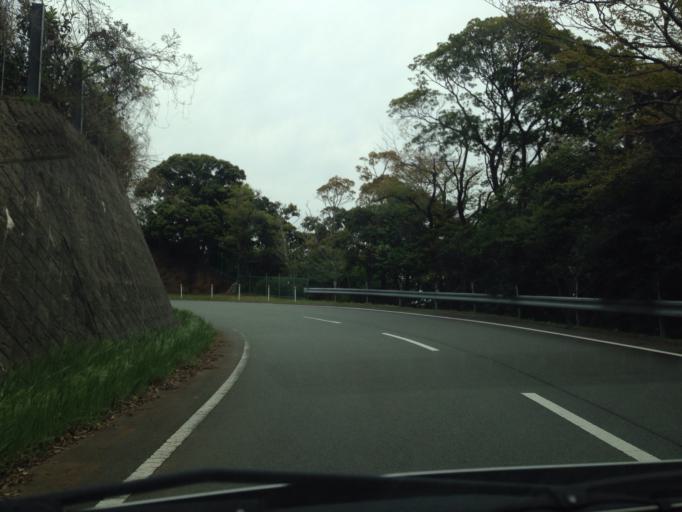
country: JP
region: Shizuoka
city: Heda
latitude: 35.0229
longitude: 138.7975
